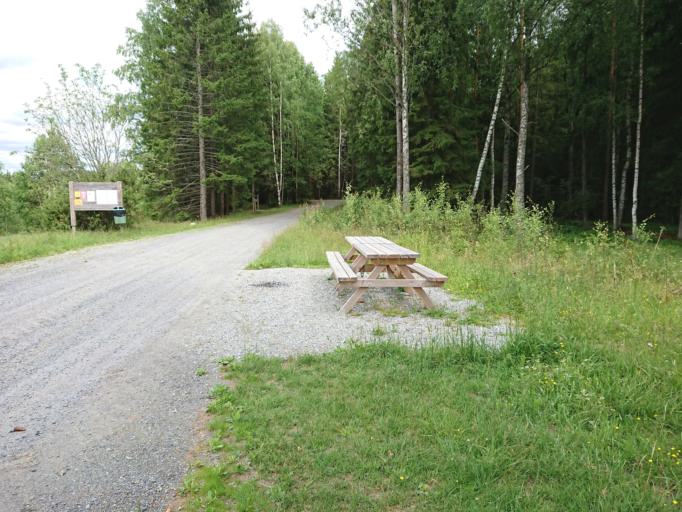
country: NO
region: Ostfold
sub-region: Spydeberg
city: Spydeberg
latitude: 59.6094
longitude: 11.1277
